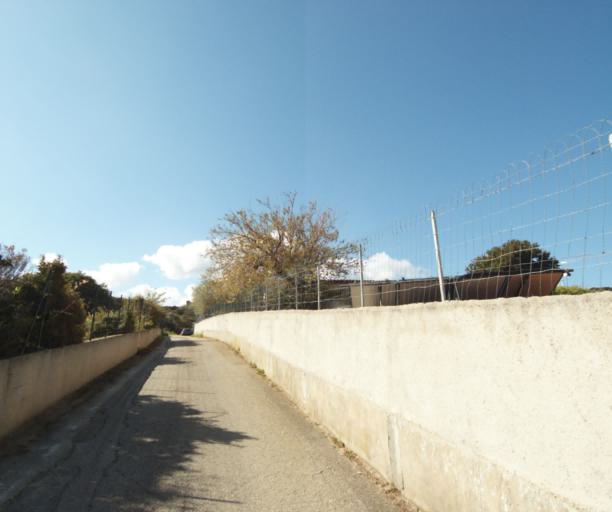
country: FR
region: Corsica
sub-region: Departement de la Corse-du-Sud
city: Propriano
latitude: 41.6693
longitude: 8.9094
